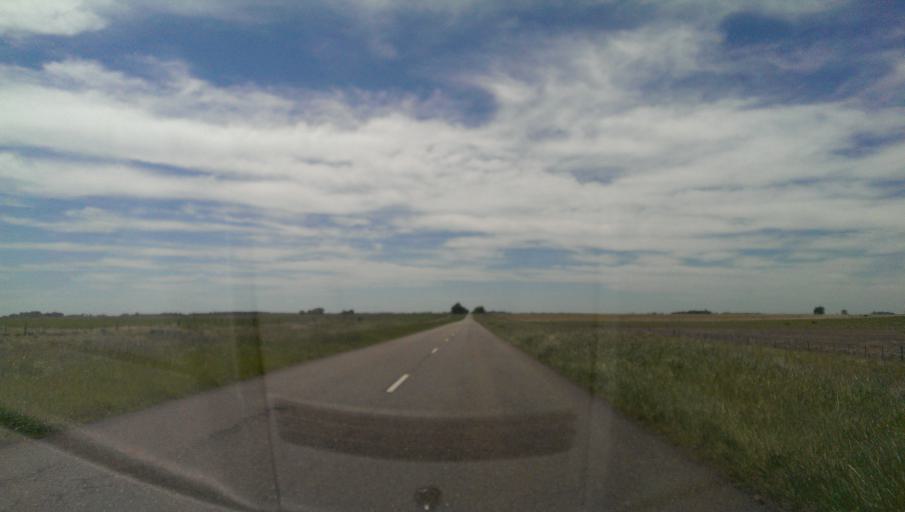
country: AR
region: Buenos Aires
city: Coronel Pringles
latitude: -37.7157
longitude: -61.5924
